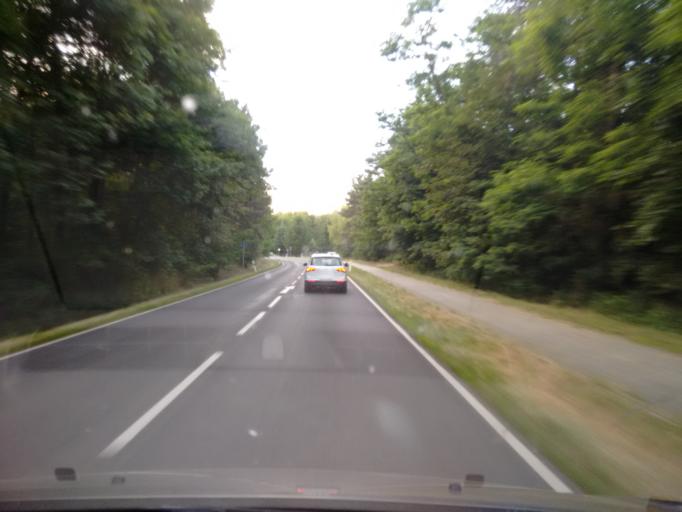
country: DE
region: Brandenburg
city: Mixdorf
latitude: 52.1450
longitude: 14.4158
